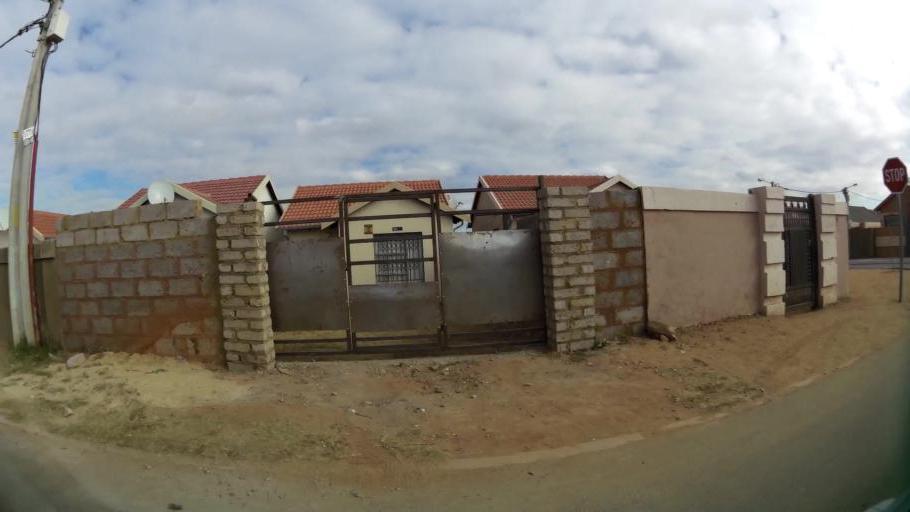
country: ZA
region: Gauteng
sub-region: City of Johannesburg Metropolitan Municipality
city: Roodepoort
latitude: -26.1932
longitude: 27.9117
